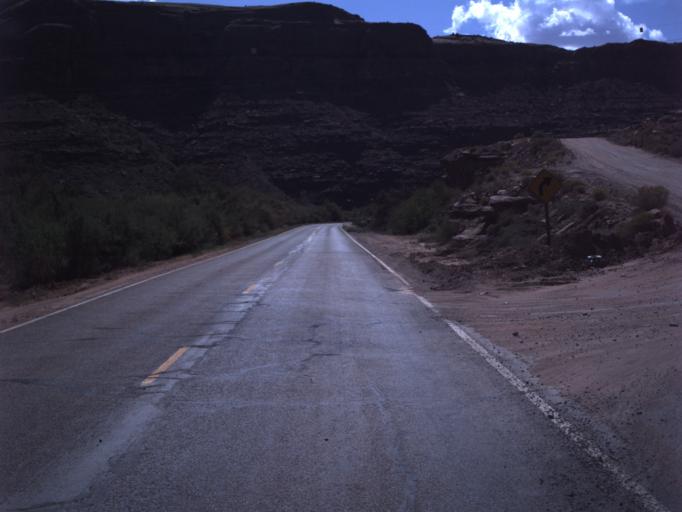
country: US
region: Utah
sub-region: Grand County
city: Moab
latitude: 38.5335
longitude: -109.6075
